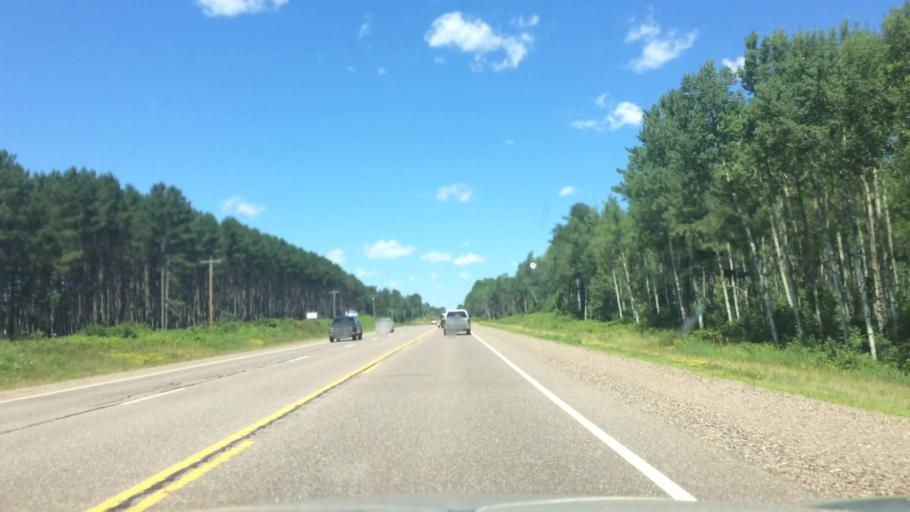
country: US
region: Wisconsin
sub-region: Lincoln County
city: Tomahawk
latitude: 45.6693
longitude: -89.7140
